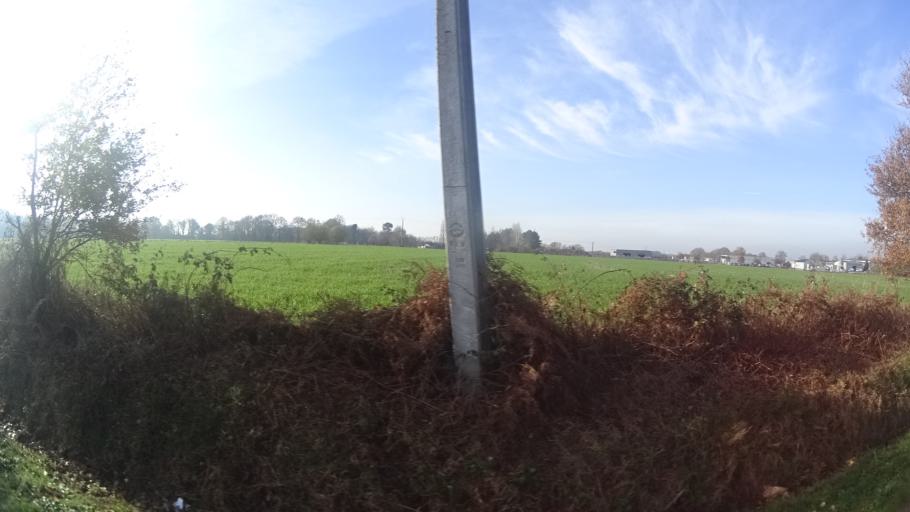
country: FR
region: Brittany
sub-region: Departement du Morbihan
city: Allaire
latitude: 47.6258
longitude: -2.1592
